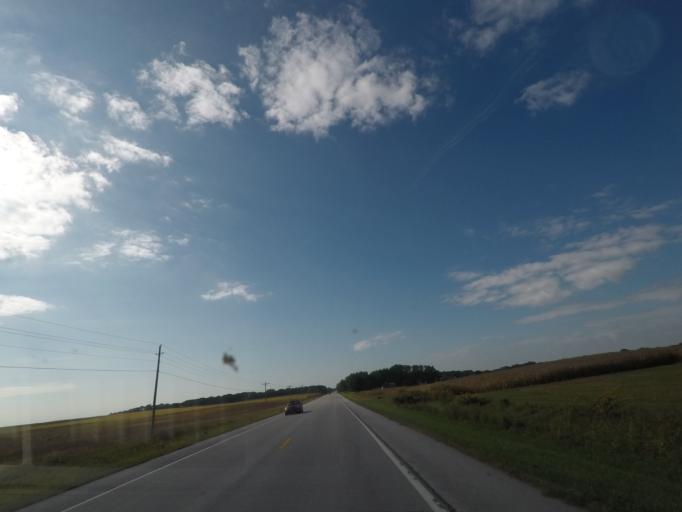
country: US
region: Iowa
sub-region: Story County
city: Nevada
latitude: 41.9995
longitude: -93.4446
